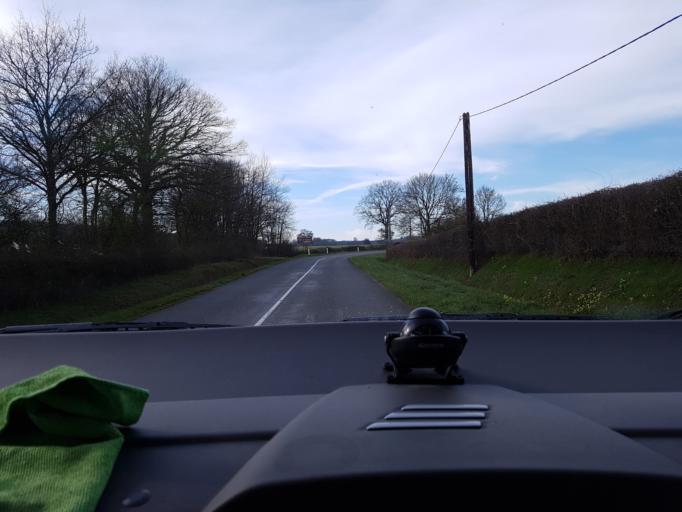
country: FR
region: Bourgogne
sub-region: Departement de Saone-et-Loire
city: Toulon-sur-Arroux
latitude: 46.7510
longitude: 4.1305
